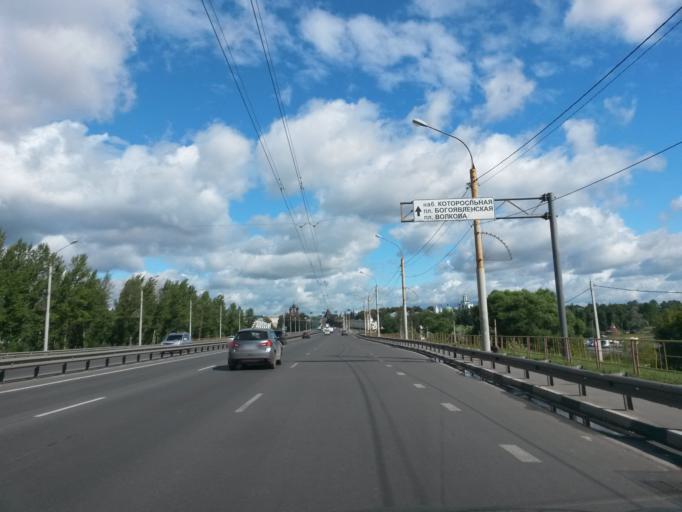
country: RU
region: Jaroslavl
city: Yaroslavl
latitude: 57.6155
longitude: 39.8844
